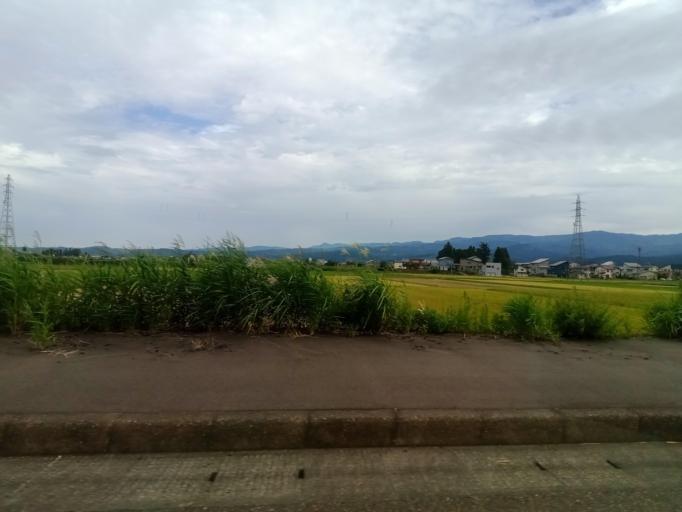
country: JP
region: Niigata
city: Arai
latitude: 37.0589
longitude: 138.2457
